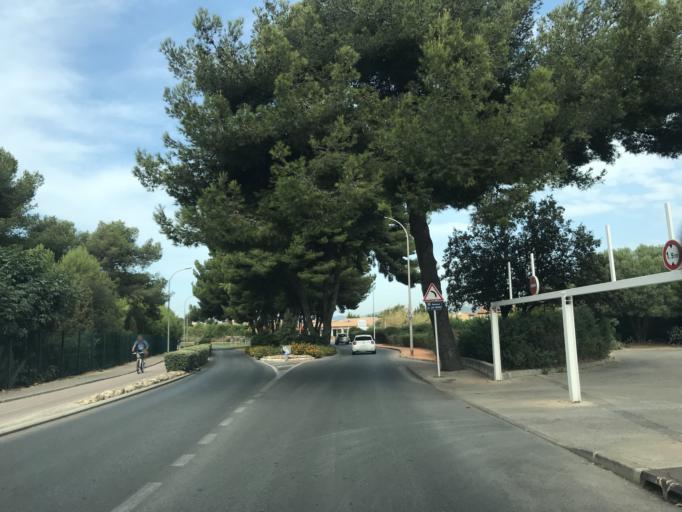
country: FR
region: Provence-Alpes-Cote d'Azur
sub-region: Departement du Var
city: Sanary-sur-Mer
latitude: 43.0989
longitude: 5.8204
